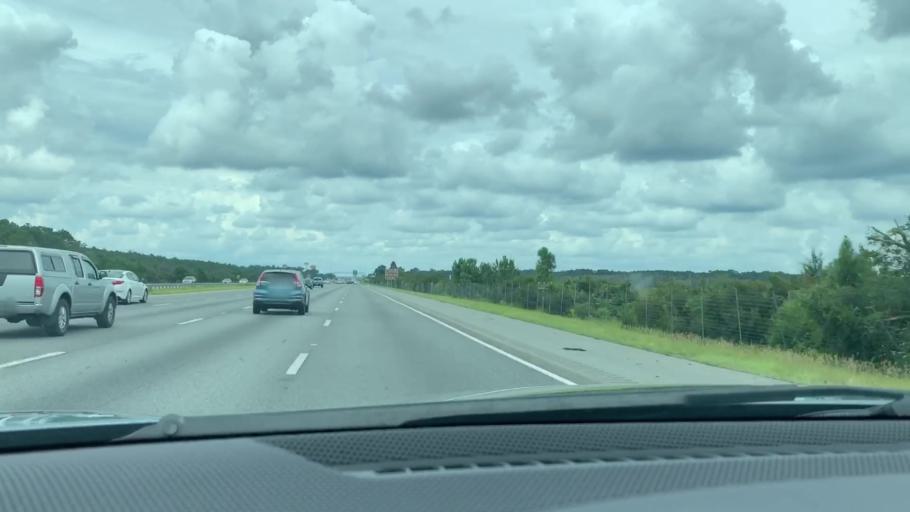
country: US
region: Georgia
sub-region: McIntosh County
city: Darien
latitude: 31.3785
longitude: -81.4535
